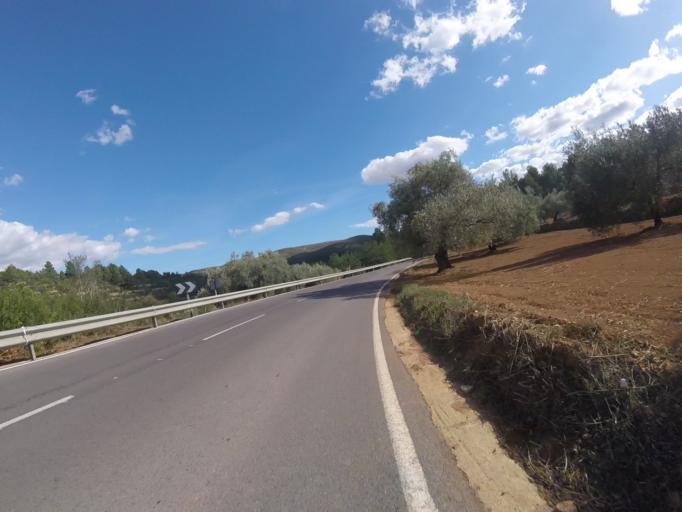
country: ES
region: Valencia
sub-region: Provincia de Castello
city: Cuevas de Vinroma
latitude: 40.3047
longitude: 0.1631
